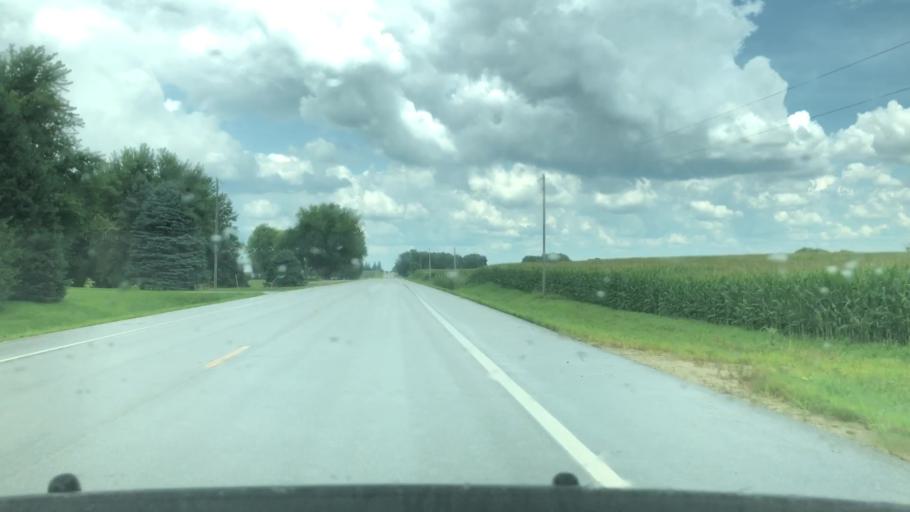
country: US
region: Minnesota
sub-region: Olmsted County
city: Stewartville
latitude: 43.9032
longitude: -92.5284
